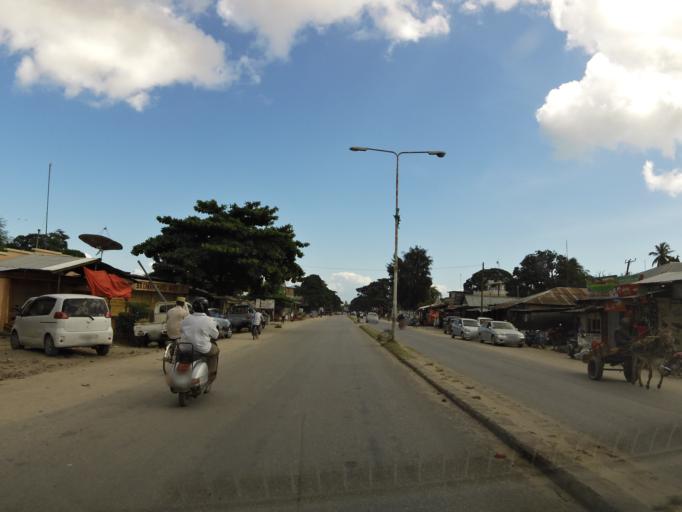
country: TZ
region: Zanzibar Urban/West
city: Zanzibar
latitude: -6.1642
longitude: 39.2217
